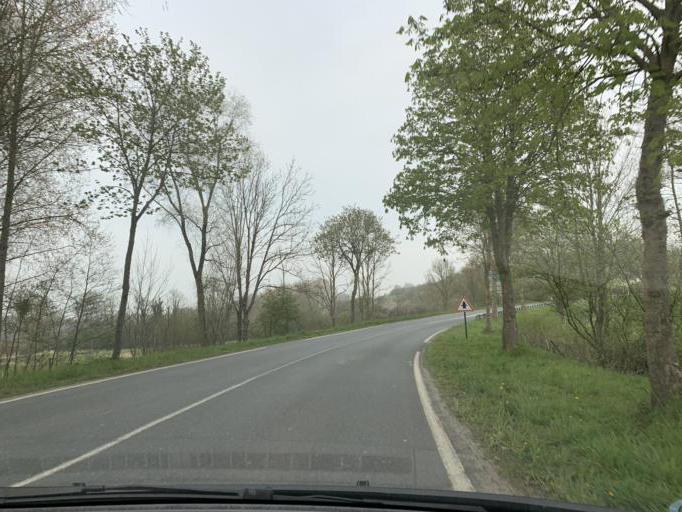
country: FR
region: Nord-Pas-de-Calais
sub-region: Departement du Pas-de-Calais
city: Montreuil
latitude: 50.4805
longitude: 1.7715
